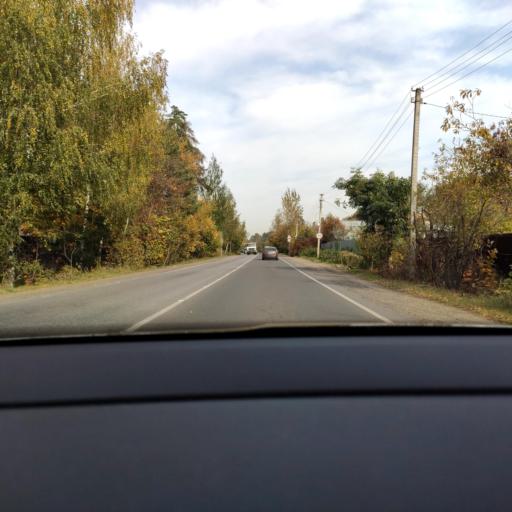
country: RU
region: Moskovskaya
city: Lesnyye Polyany
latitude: 55.9683
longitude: 37.8716
